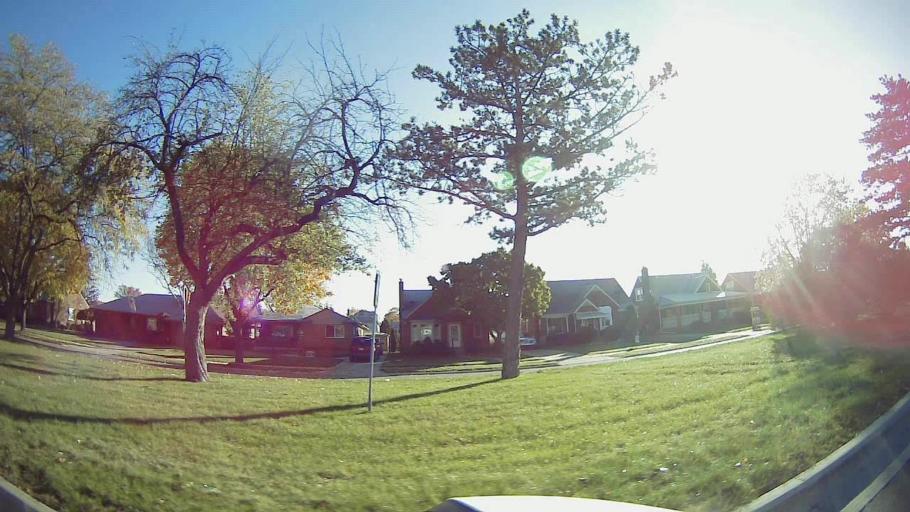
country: US
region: Michigan
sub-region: Wayne County
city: Dearborn
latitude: 42.3323
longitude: -83.1692
